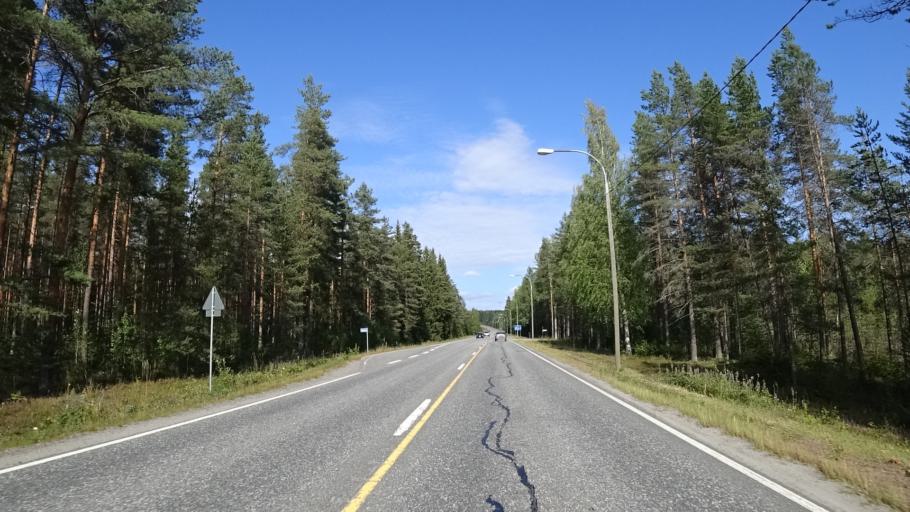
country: FI
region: North Karelia
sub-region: Joensuu
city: Eno
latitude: 62.7754
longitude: 30.0587
